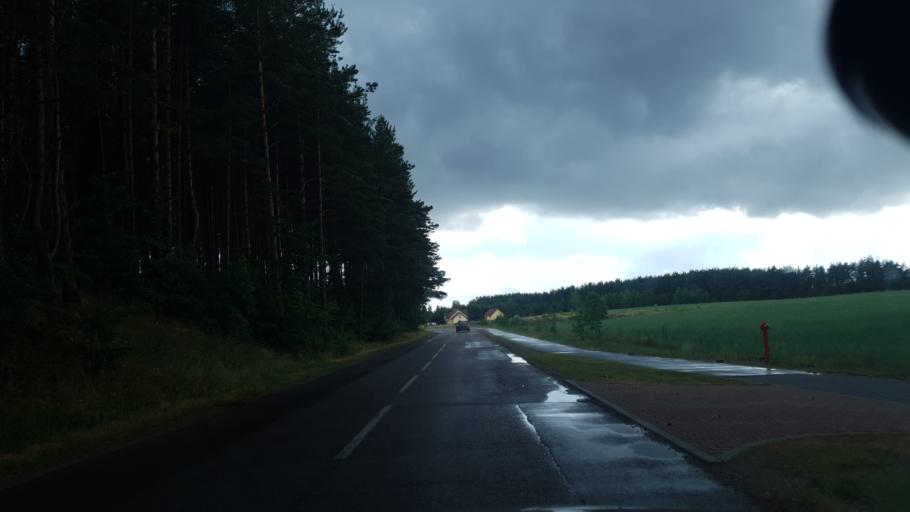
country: PL
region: Pomeranian Voivodeship
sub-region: Powiat kartuski
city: Stezyca
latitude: 54.2177
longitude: 17.9629
